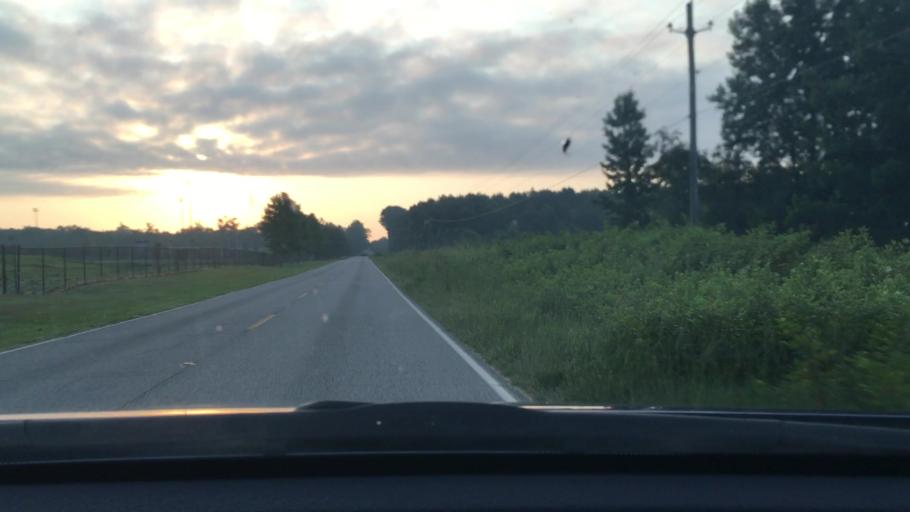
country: US
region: South Carolina
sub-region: Darlington County
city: Hartsville
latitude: 34.3503
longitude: -80.0906
